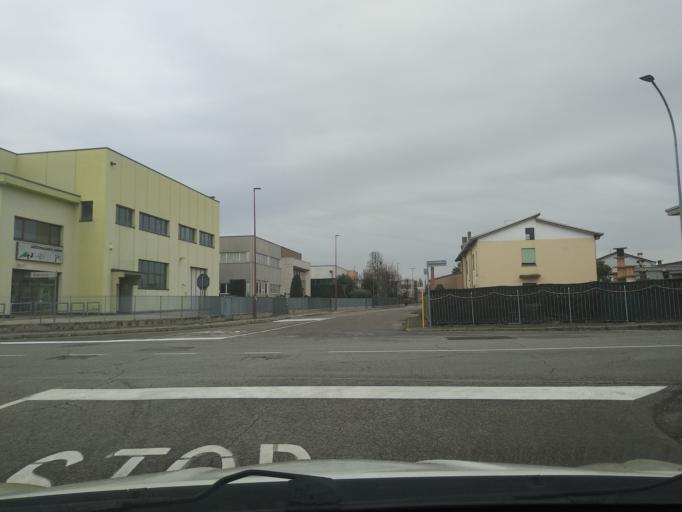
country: IT
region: Veneto
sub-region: Provincia di Padova
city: Rubano
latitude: 45.4216
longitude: 11.7949
